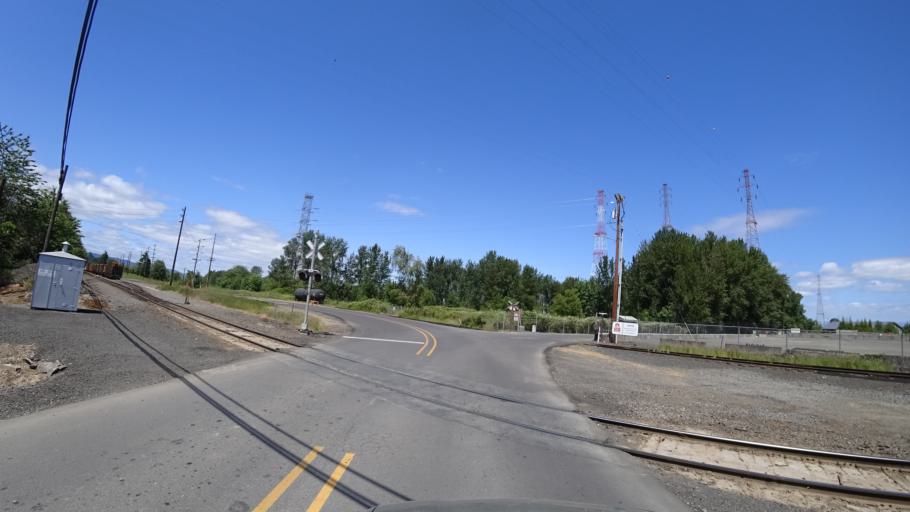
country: US
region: Oregon
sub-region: Washington County
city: Oak Hills
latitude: 45.6112
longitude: -122.7956
